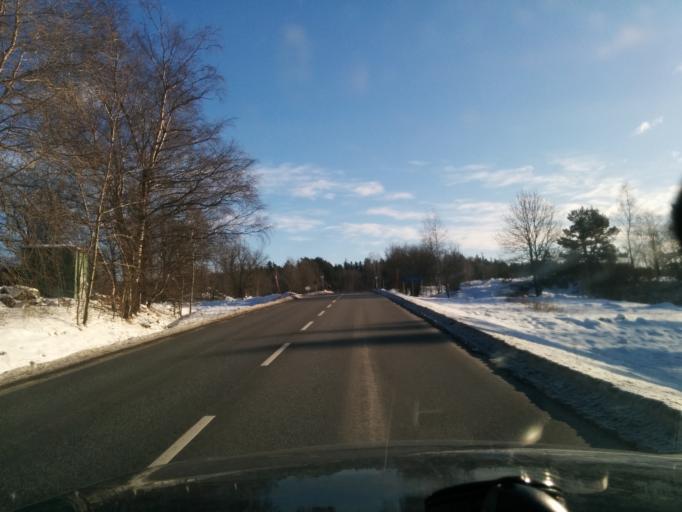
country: SE
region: Stockholm
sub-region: Taby Kommun
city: Taby
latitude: 59.4856
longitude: 18.0851
